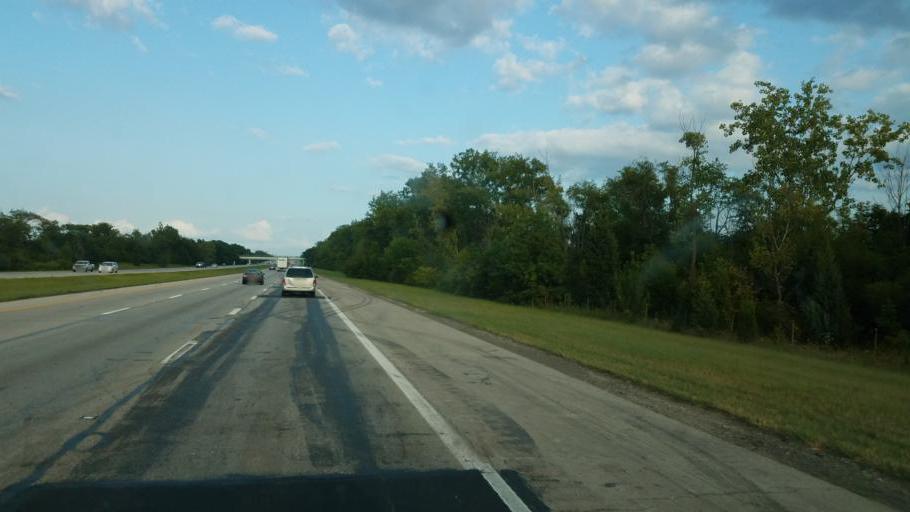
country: US
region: Ohio
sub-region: Franklin County
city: Obetz
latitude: 39.8729
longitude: -82.9778
